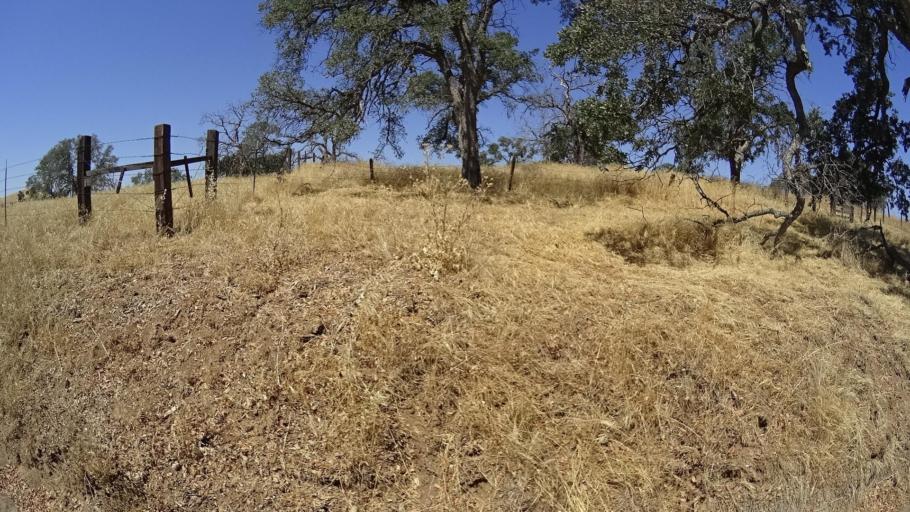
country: US
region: California
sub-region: Mariposa County
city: Mariposa
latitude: 37.3605
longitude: -119.9648
